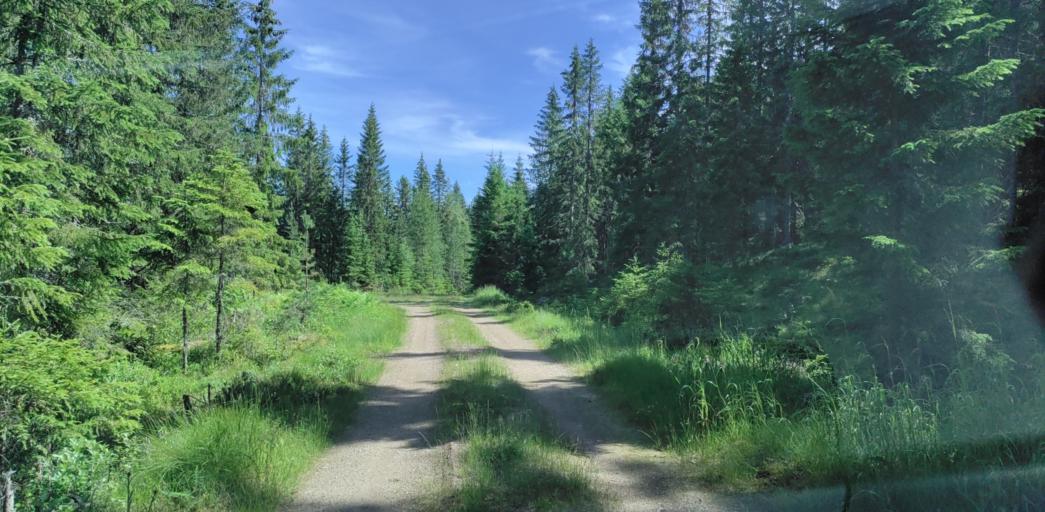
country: SE
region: Vaermland
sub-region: Hagfors Kommun
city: Ekshaerad
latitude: 60.0876
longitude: 13.3784
